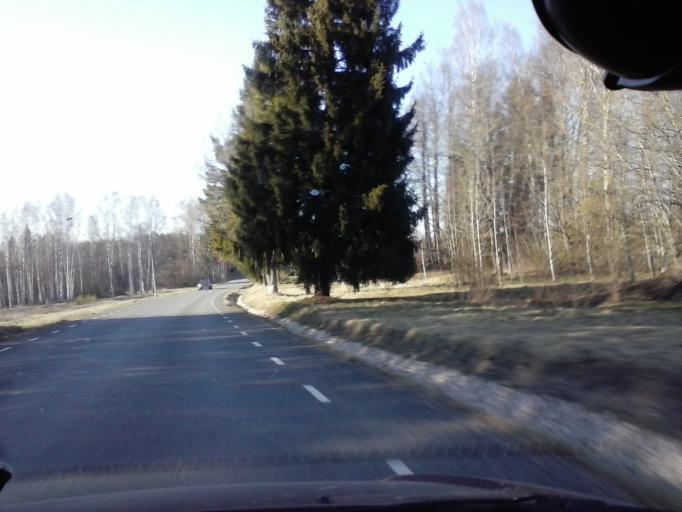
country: EE
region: Tartu
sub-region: UElenurme vald
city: Ulenurme
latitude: 58.1726
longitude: 26.8339
